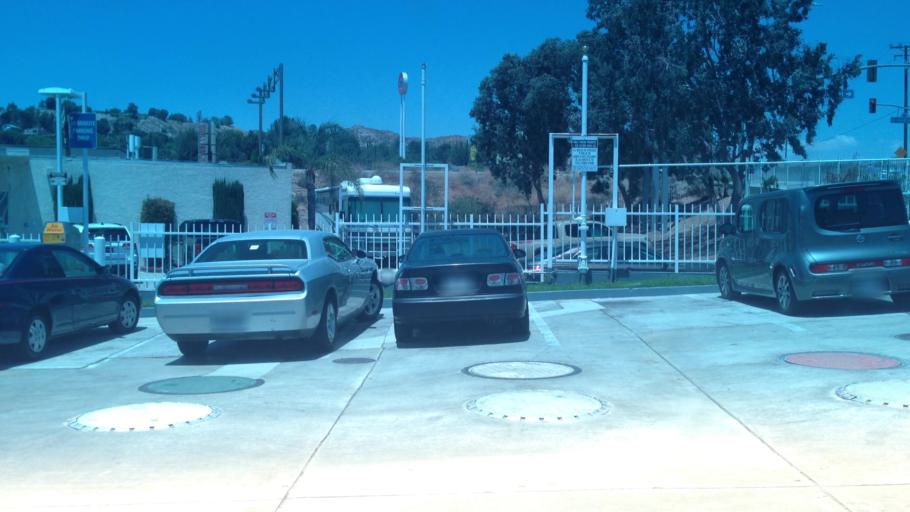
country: US
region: California
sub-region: Los Angeles County
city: Agua Dulce
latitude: 34.4240
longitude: -118.4240
